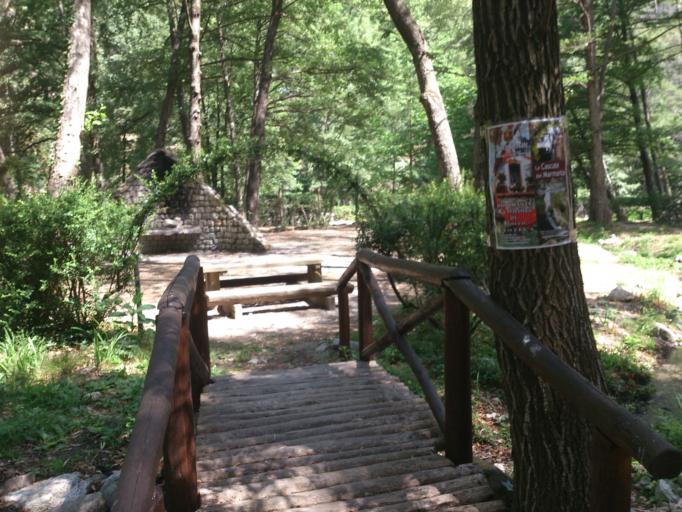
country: IT
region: Calabria
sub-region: Provincia di Reggio Calabria
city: Bivongi
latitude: 38.4867
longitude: 16.4325
